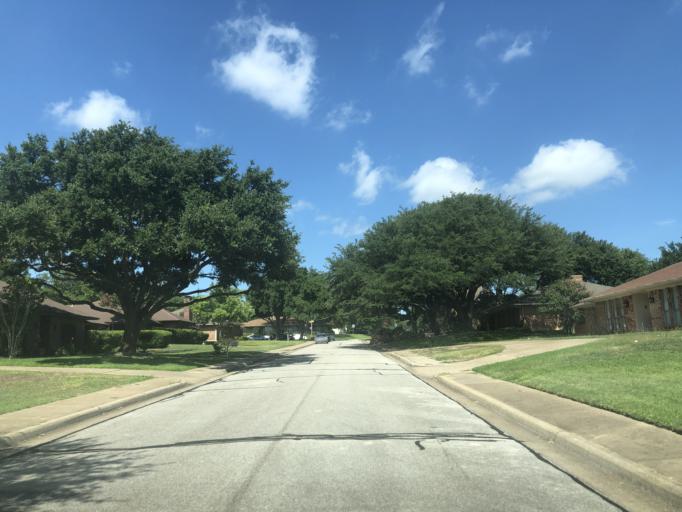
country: US
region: Texas
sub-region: Dallas County
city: Duncanville
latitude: 32.6480
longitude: -96.9326
